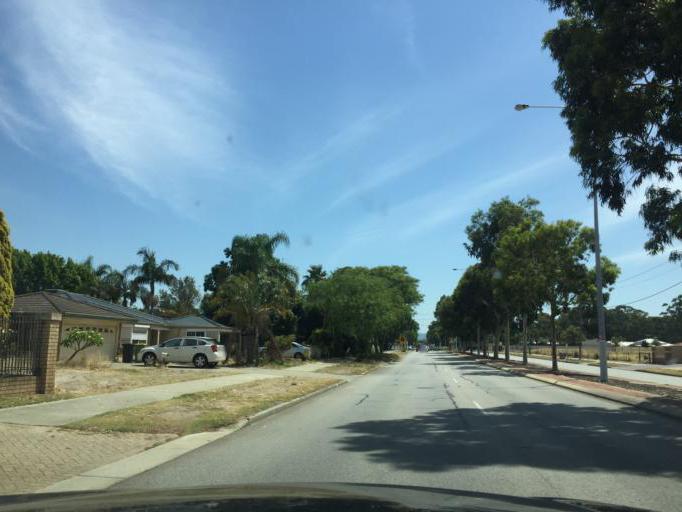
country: AU
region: Western Australia
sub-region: Gosnells
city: Thornlie
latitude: -32.0767
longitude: 115.9592
